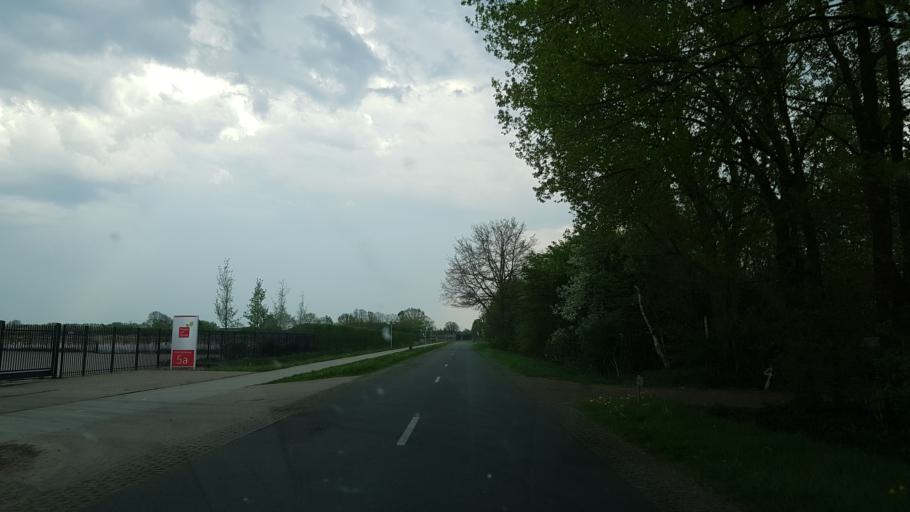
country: NL
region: North Brabant
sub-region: Gemeente Someren
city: Someren
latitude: 51.3275
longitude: 5.6946
